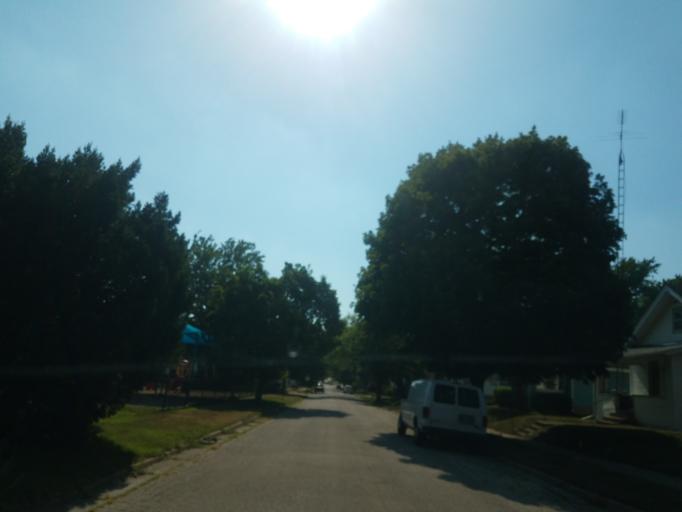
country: US
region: Illinois
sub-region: McLean County
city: Bloomington
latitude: 40.4761
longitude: -88.9770
